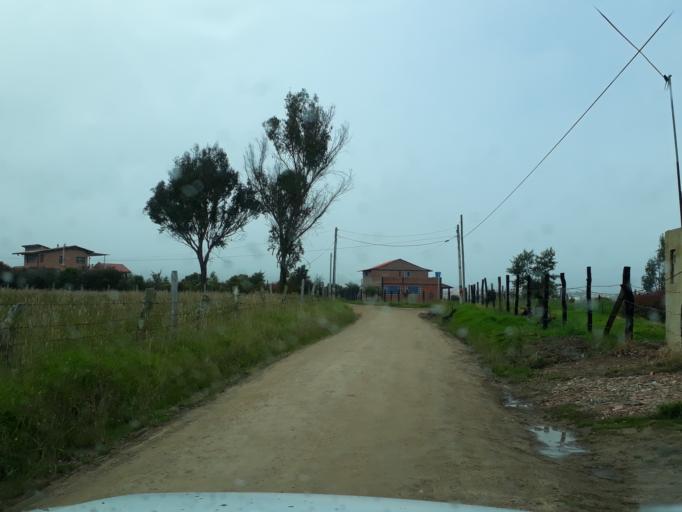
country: CO
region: Cundinamarca
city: Guasca
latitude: 4.8778
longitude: -73.8747
